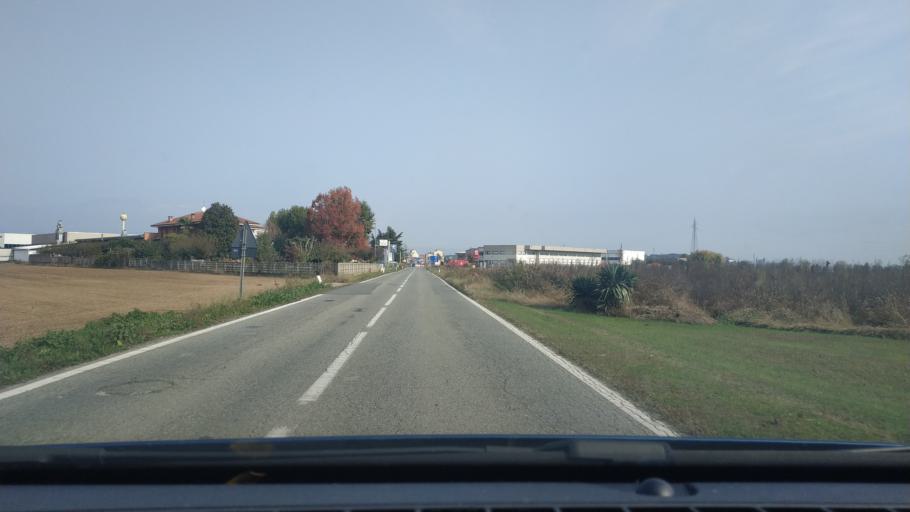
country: IT
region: Piedmont
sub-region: Provincia di Torino
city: Scarmagno
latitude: 45.3719
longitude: 7.8508
